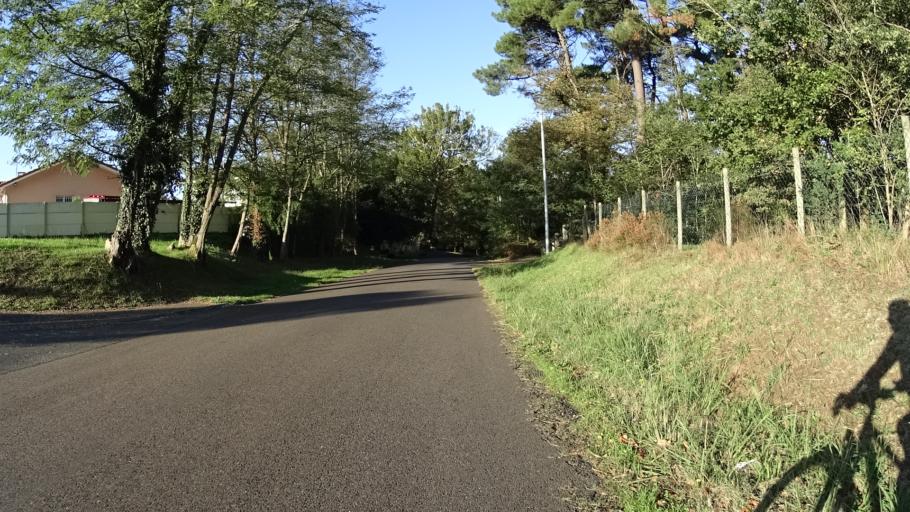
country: FR
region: Aquitaine
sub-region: Departement des Landes
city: Saint-Paul-les-Dax
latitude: 43.7345
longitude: -1.0441
